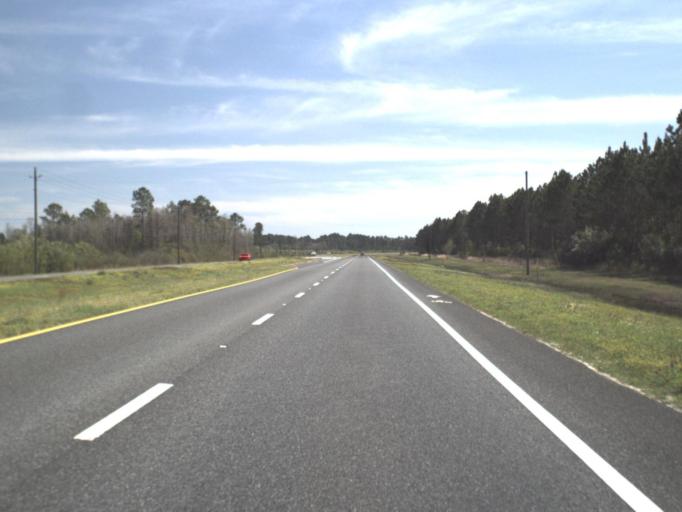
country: US
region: Florida
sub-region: Bay County
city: Lynn Haven
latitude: 30.3472
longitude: -85.6633
